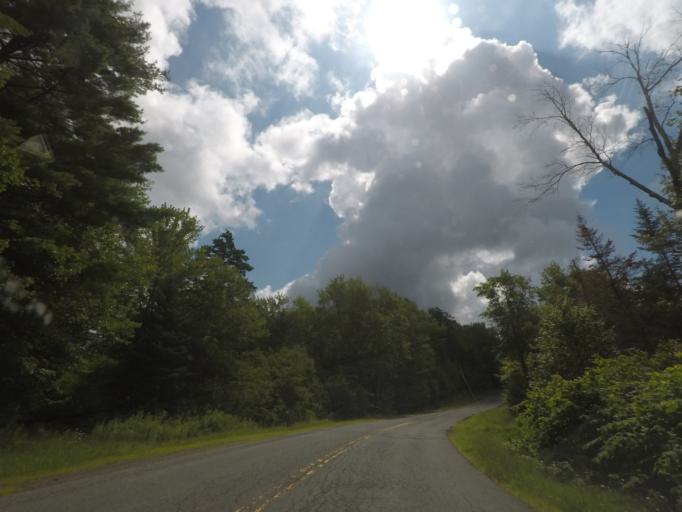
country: US
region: New York
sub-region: Rensselaer County
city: Averill Park
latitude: 42.6777
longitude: -73.4254
